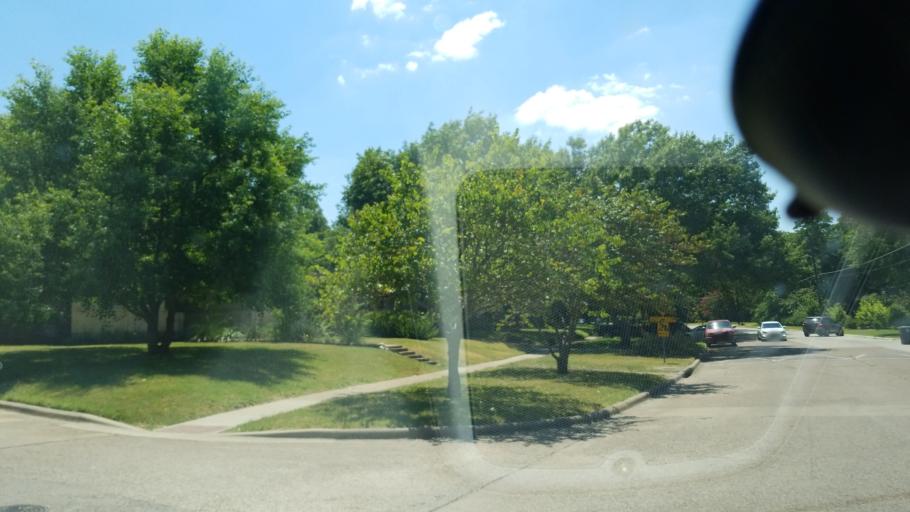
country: US
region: Texas
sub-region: Dallas County
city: Cockrell Hill
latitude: 32.7271
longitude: -96.8511
